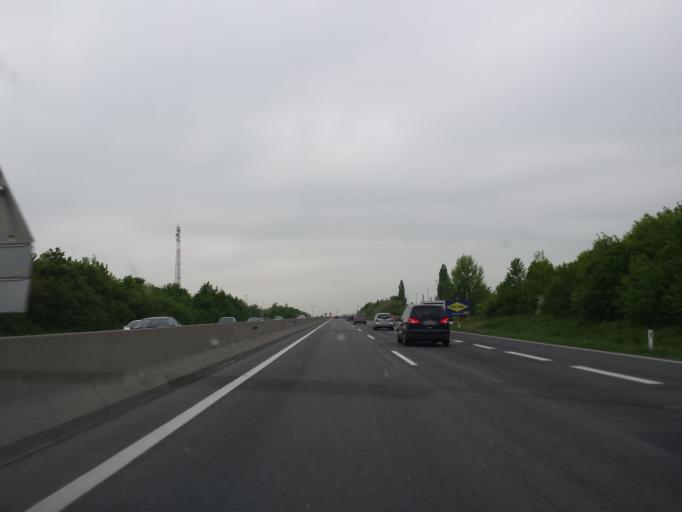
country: AT
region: Burgenland
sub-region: Politischer Bezirk Neusiedl am See
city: Zurndorf
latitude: 47.9407
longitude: 16.9619
